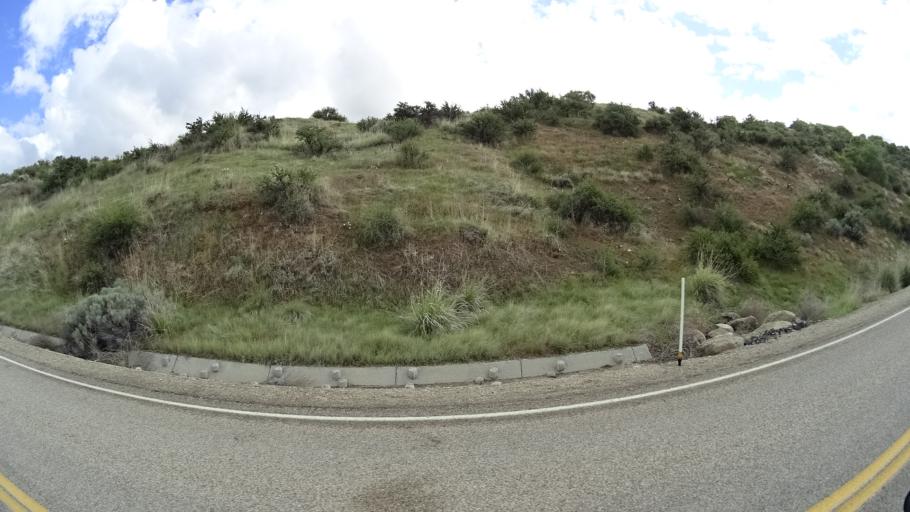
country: US
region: Idaho
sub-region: Ada County
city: Garden City
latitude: 43.7222
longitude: -116.2349
